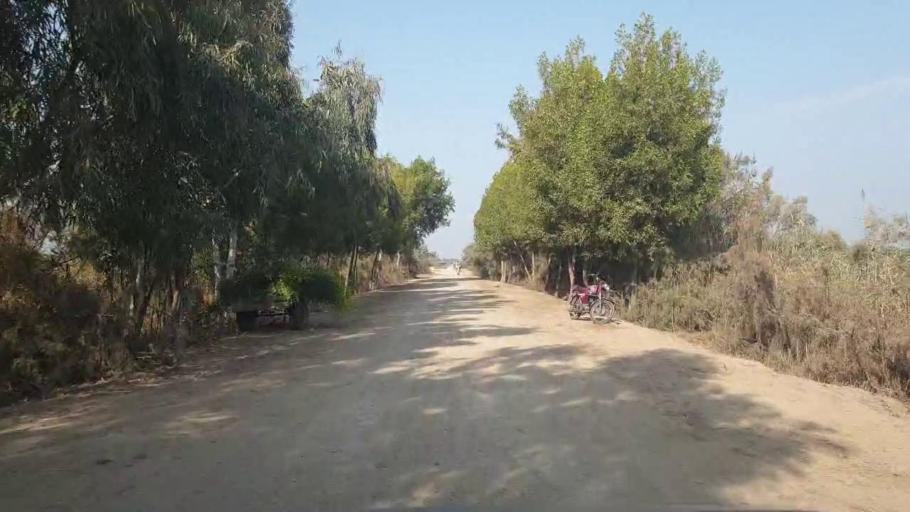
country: PK
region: Sindh
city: Tando Adam
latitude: 25.7982
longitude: 68.5923
